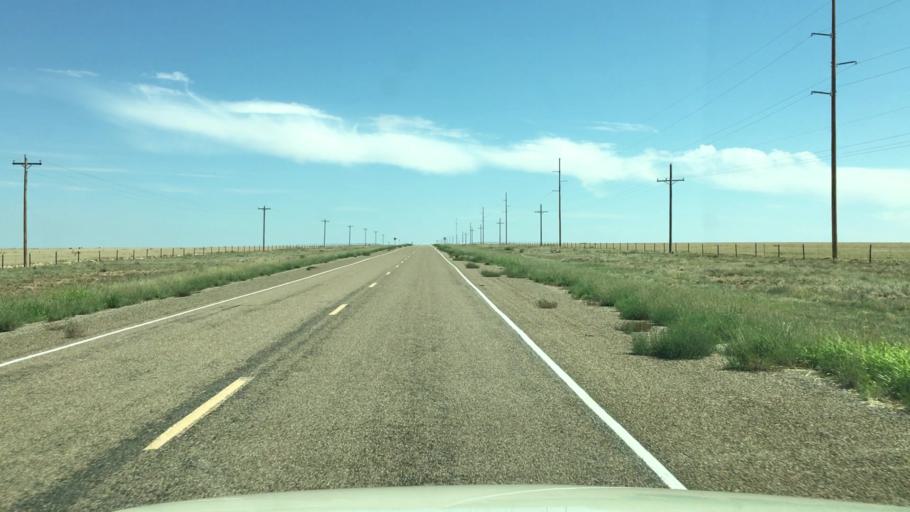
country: US
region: New Mexico
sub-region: Chaves County
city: Roswell
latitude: 33.9417
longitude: -104.5922
